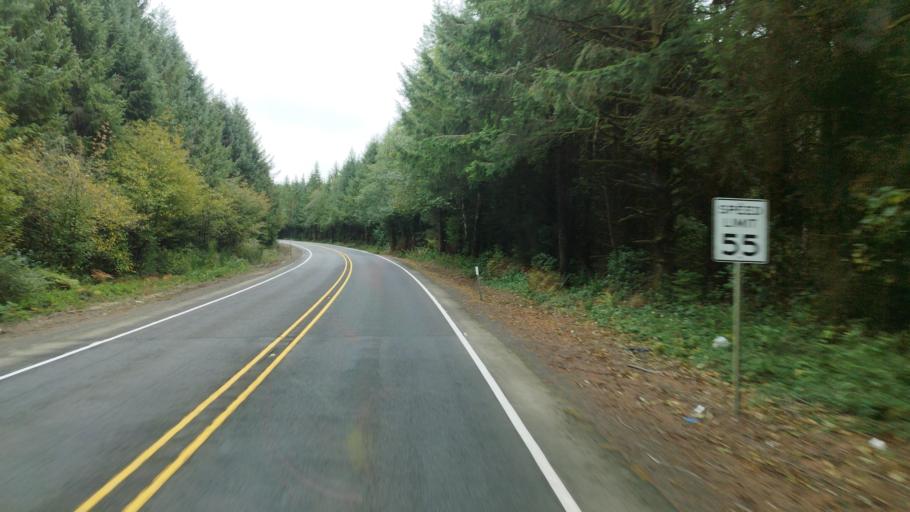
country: US
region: Oregon
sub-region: Clatsop County
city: Cannon Beach
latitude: 45.9010
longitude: -123.8655
